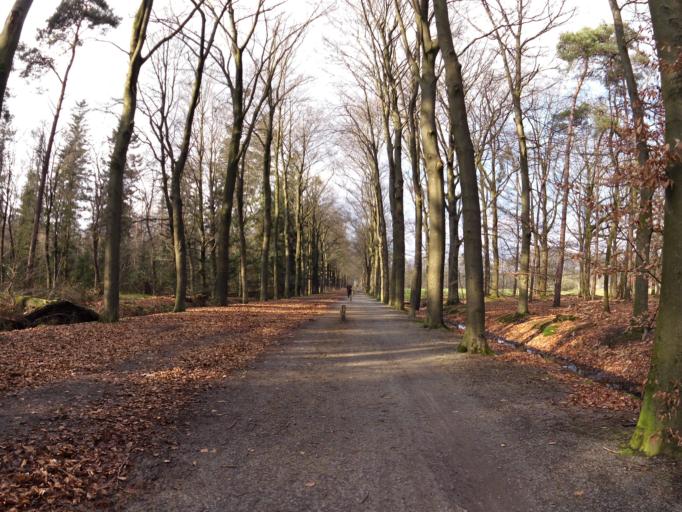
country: NL
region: North Brabant
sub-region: Gemeente Boxtel
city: Boxtel
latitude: 51.6078
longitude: 5.3106
